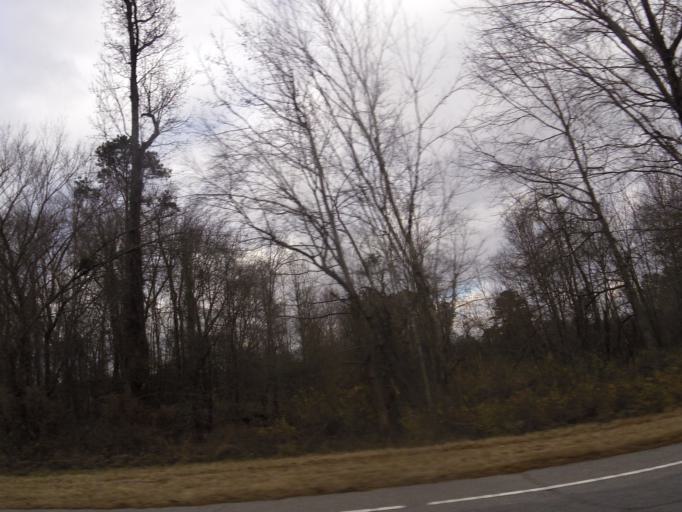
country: US
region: North Carolina
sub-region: Edgecombe County
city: Pinetops
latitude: 35.8566
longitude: -77.6874
